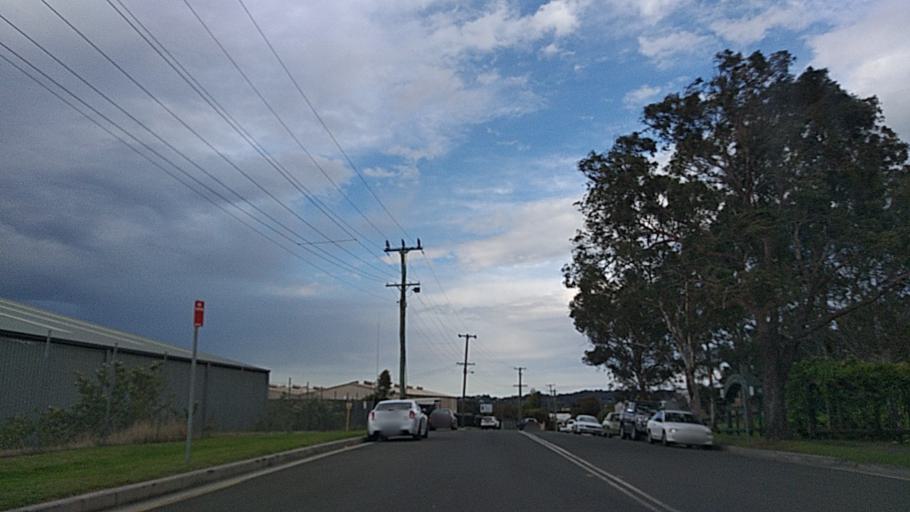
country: AU
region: New South Wales
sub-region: Wollongong
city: Cordeaux Heights
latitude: -34.4592
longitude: 150.8457
